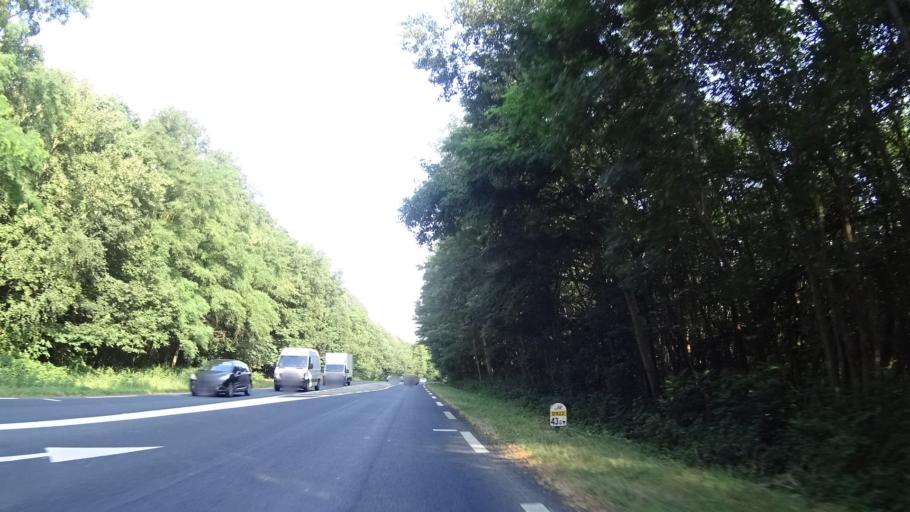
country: FR
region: Ile-de-France
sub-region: Departement du Val-d'Oise
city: Seugy
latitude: 49.1248
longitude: 2.3989
